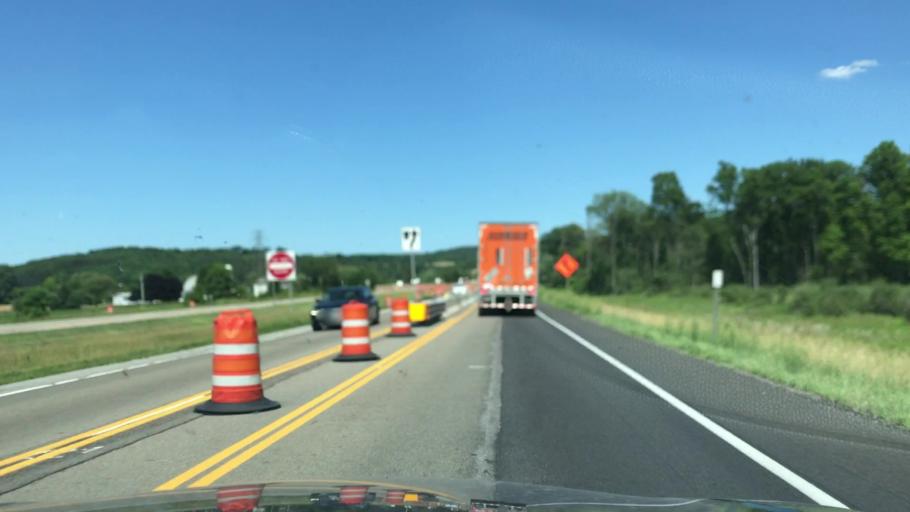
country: US
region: New York
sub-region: Steuben County
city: Wayland
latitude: 42.5385
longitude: -77.6038
